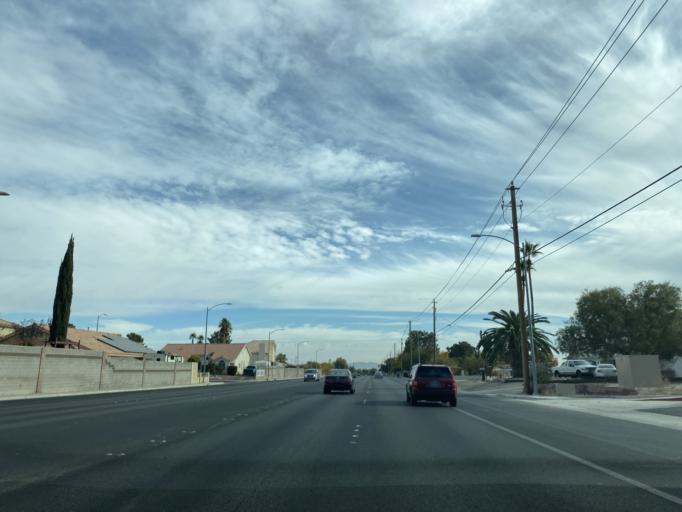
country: US
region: Nevada
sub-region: Clark County
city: Las Vegas
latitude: 36.2470
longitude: -115.2333
